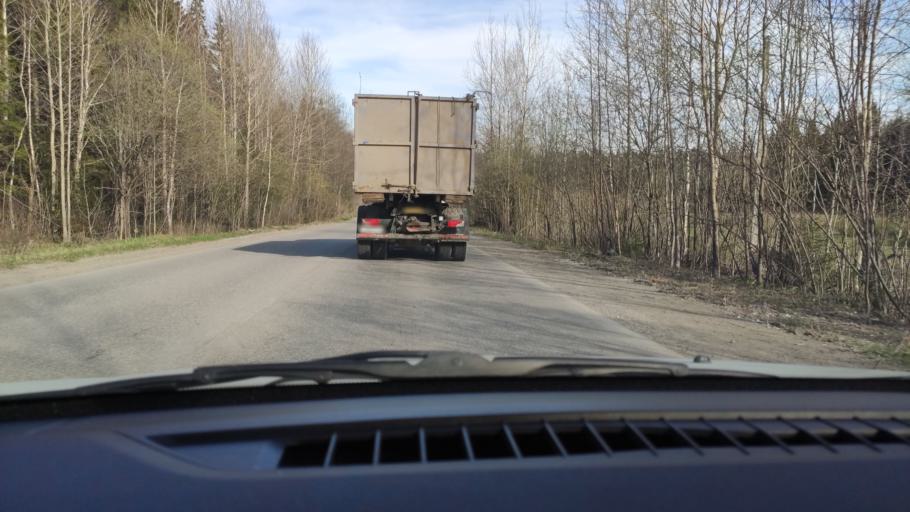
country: RU
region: Perm
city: Ferma
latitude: 57.9372
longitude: 56.4622
